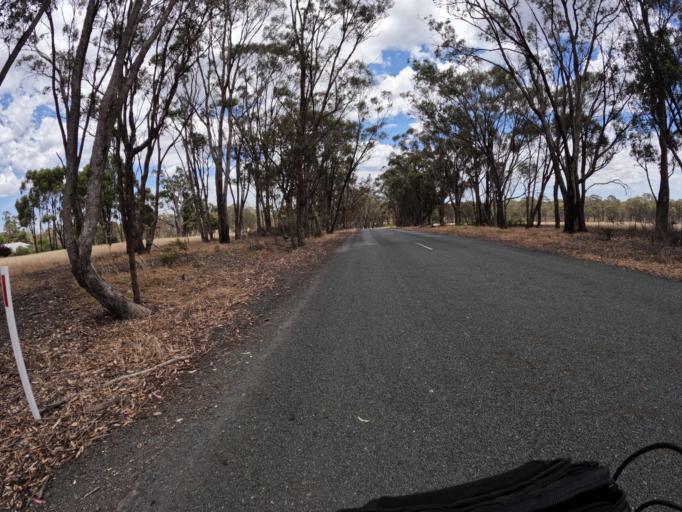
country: AU
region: Victoria
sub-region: Greater Shepparton
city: Shepparton
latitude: -36.6826
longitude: 145.1902
